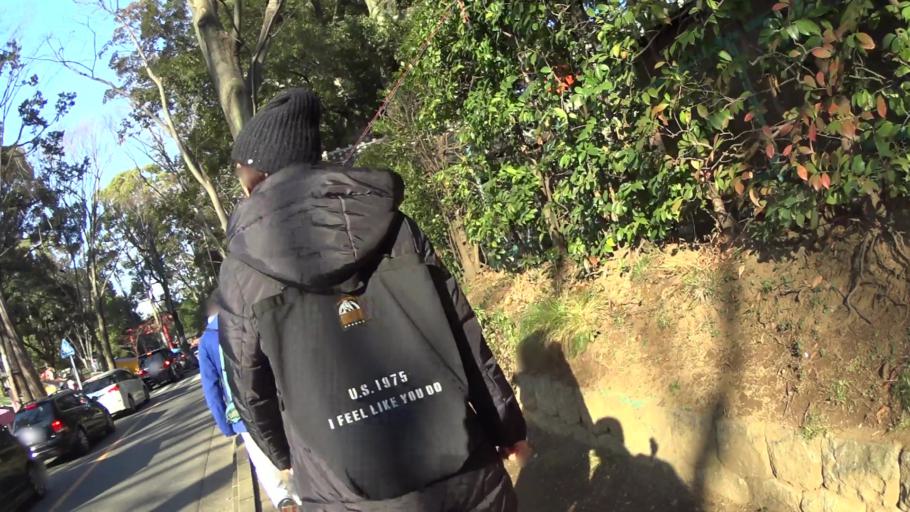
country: JP
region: Saitama
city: Saitama
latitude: 35.9145
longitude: 139.6311
